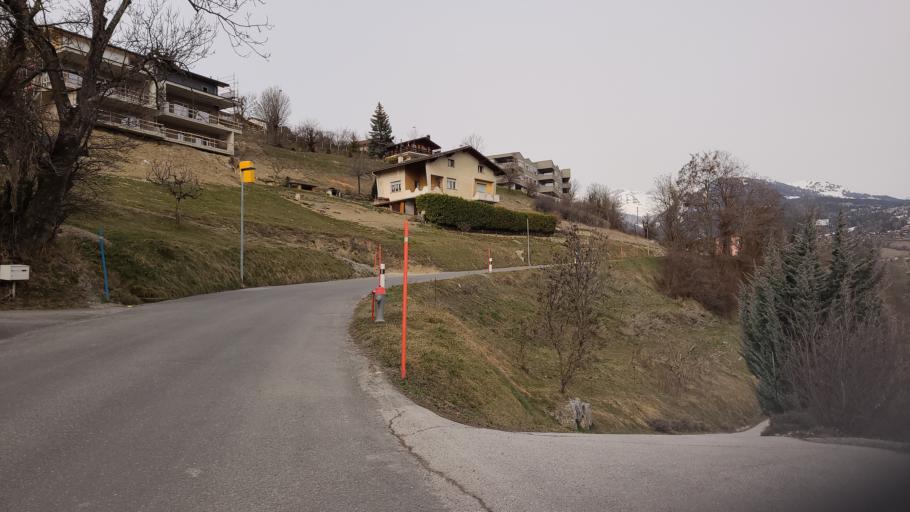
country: CH
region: Valais
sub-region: Herens District
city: Ayent
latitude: 46.2780
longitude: 7.4122
